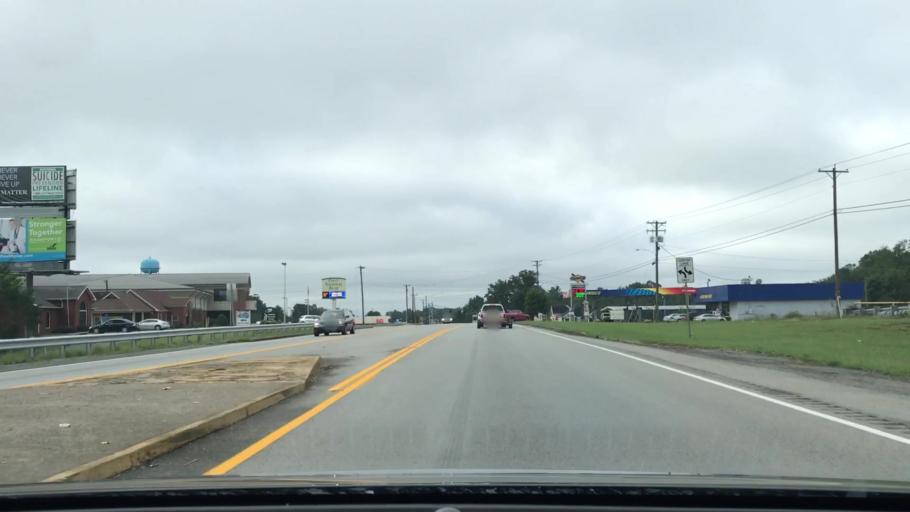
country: US
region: Kentucky
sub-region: Russell County
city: Russell Springs
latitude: 37.0370
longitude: -85.0751
